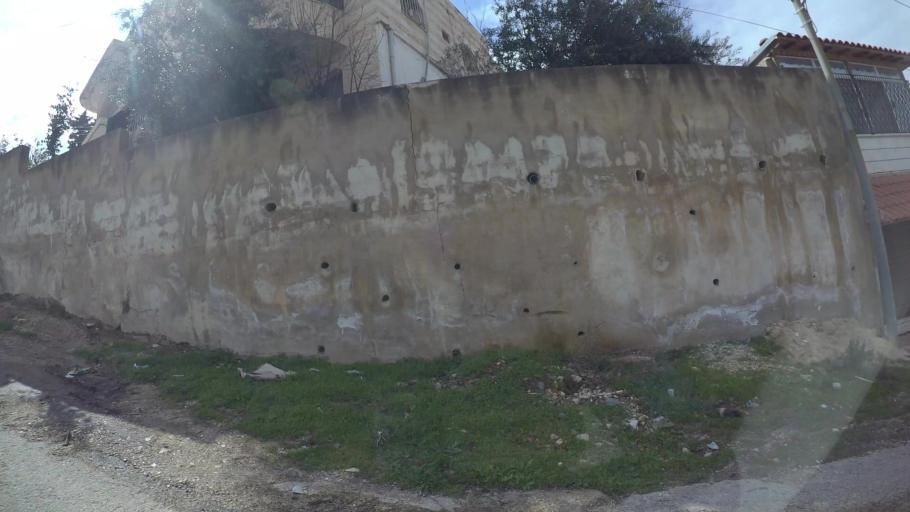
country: JO
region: Amman
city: Al Jubayhah
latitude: 32.0353
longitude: 35.8262
